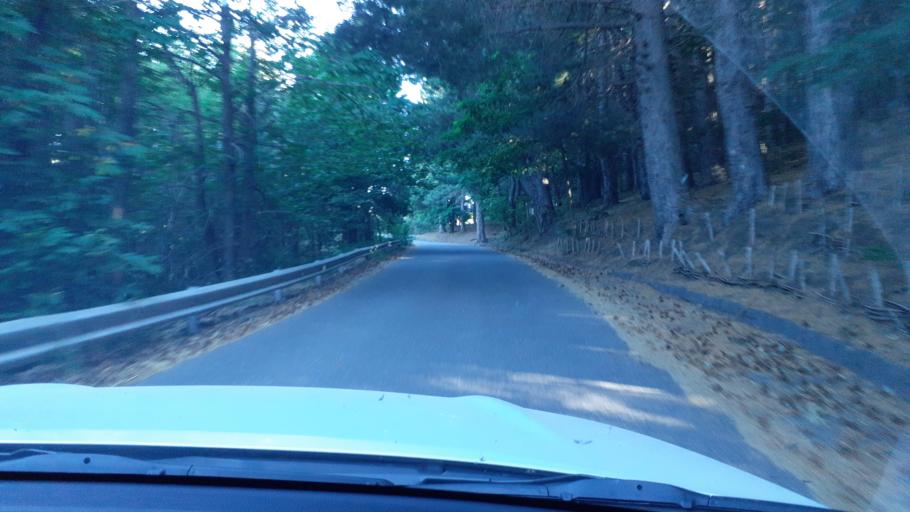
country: IT
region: Sicily
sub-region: Catania
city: Ragalna
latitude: 37.6878
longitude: 14.9819
